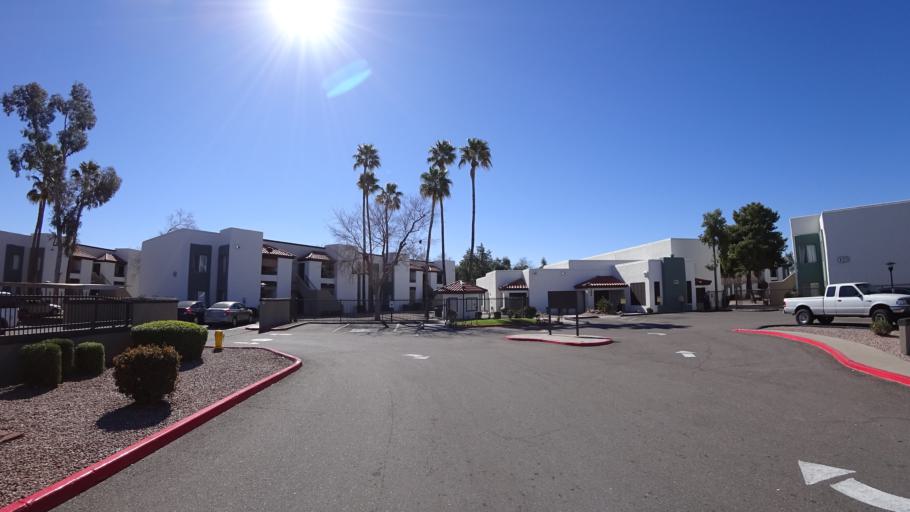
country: US
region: Arizona
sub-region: Maricopa County
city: Mesa
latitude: 33.4079
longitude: -111.7864
